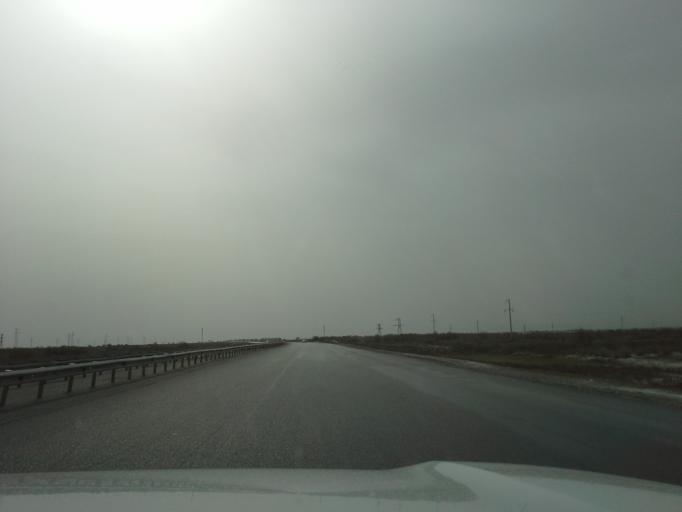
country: TM
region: Ahal
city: Kaka
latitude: 37.4874
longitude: 59.4718
